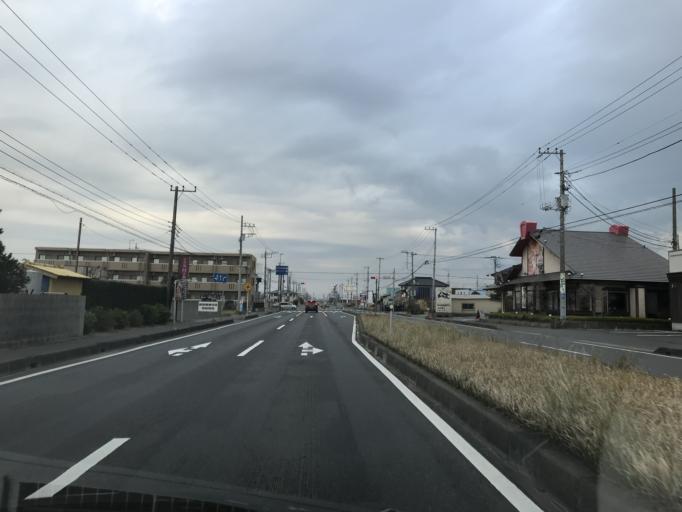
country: JP
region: Chiba
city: Omigawa
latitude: 35.8590
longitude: 140.7004
